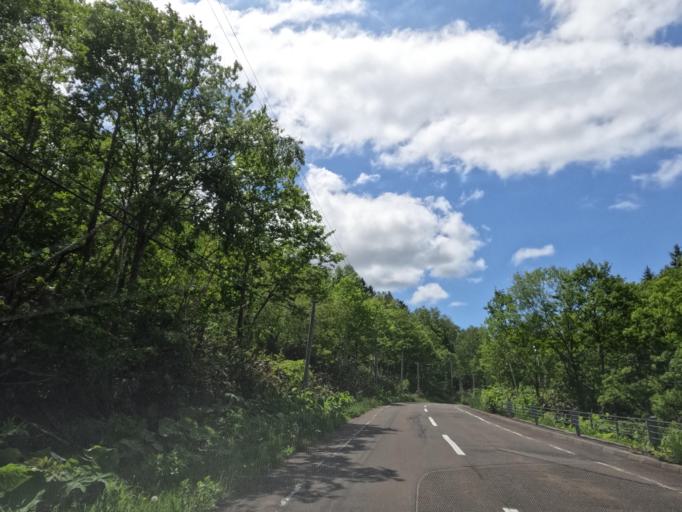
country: JP
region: Hokkaido
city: Sunagawa
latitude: 43.5080
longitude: 141.6050
